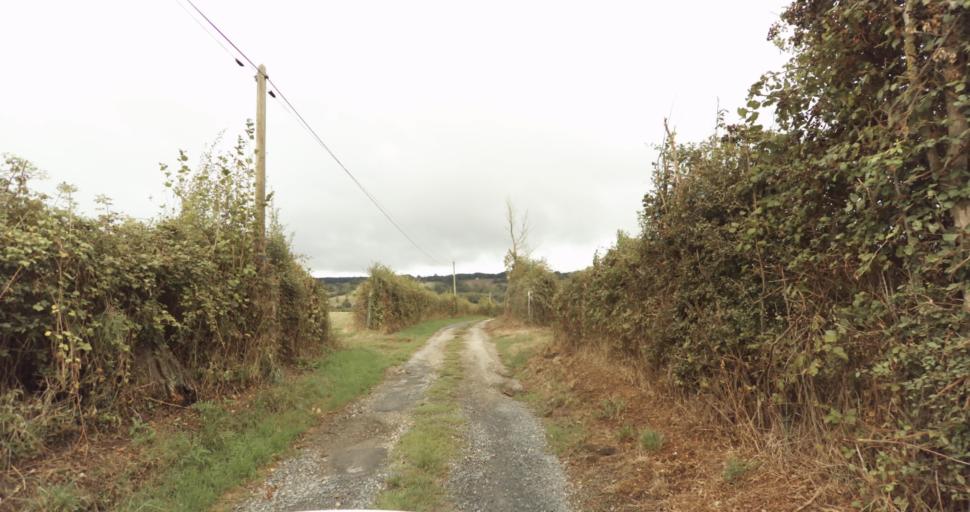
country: FR
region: Lower Normandy
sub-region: Departement du Calvados
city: Livarot
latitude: 48.9311
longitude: 0.1075
